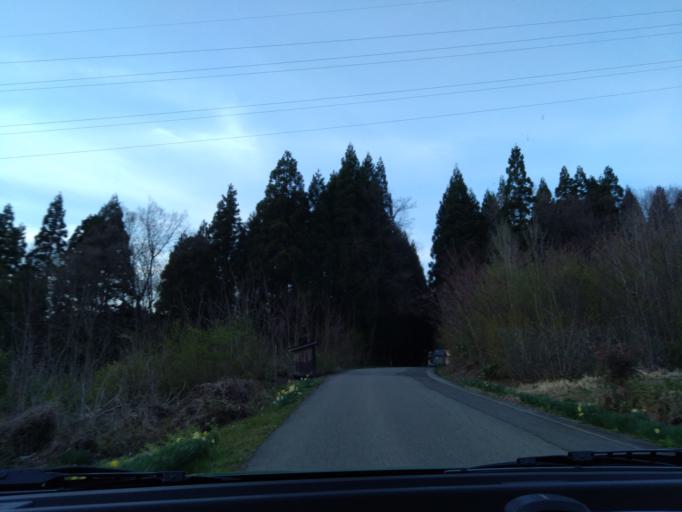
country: JP
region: Akita
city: Kakunodatemachi
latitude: 39.5907
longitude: 140.5778
